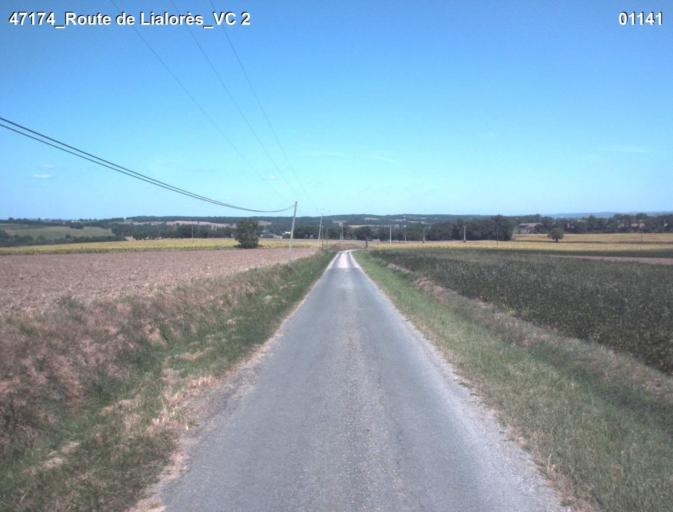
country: FR
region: Midi-Pyrenees
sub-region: Departement du Gers
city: Condom
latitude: 44.0162
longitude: 0.3762
